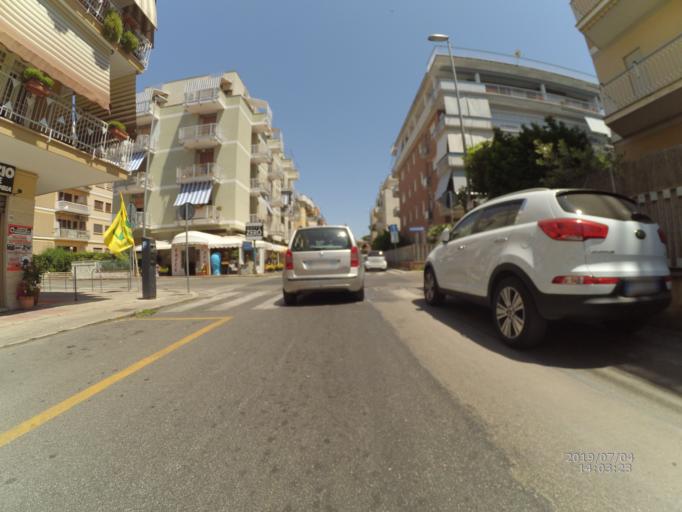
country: IT
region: Latium
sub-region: Provincia di Latina
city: Terracina
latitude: 41.2864
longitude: 13.2399
